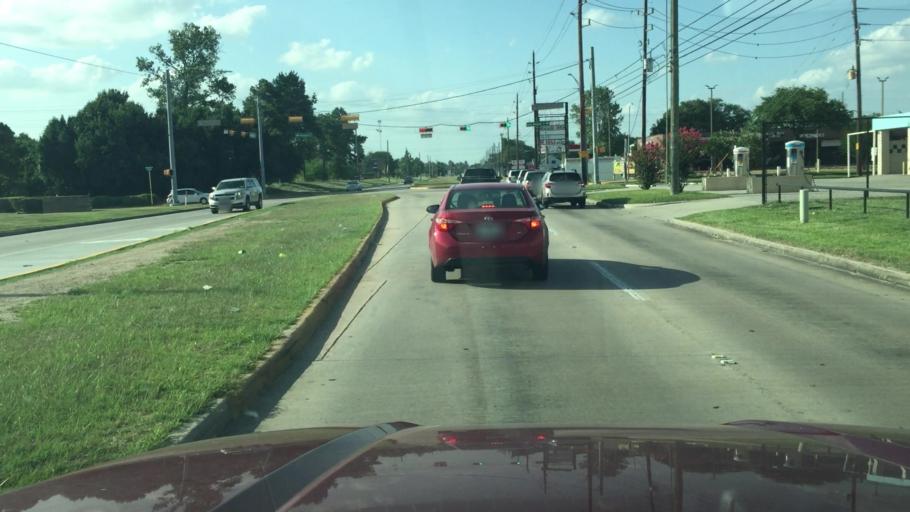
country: US
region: Texas
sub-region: Harris County
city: Hudson
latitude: 29.9515
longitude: -95.4982
